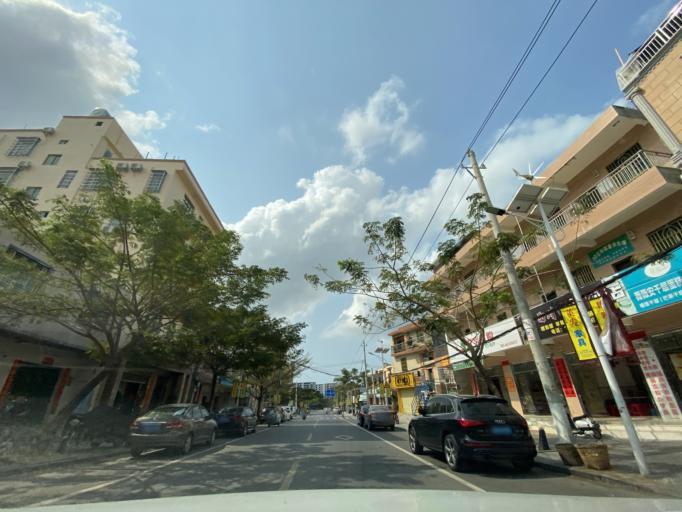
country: CN
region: Hainan
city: Yingzhou
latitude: 18.4208
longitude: 109.8500
